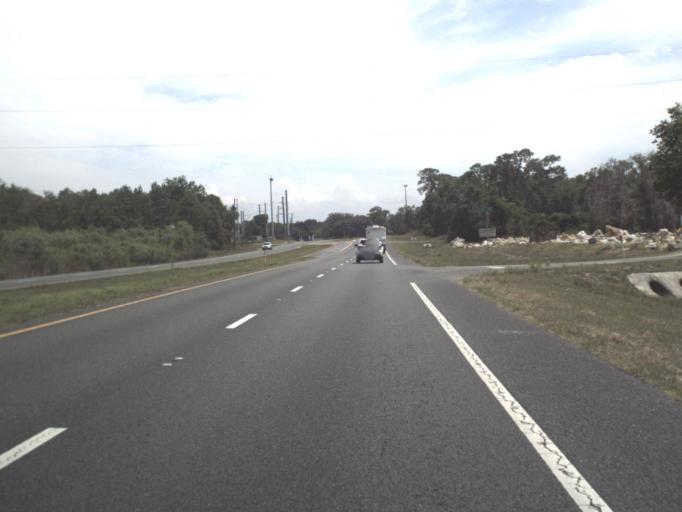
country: US
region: Florida
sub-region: Sumter County
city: Wildwood
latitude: 28.8271
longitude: -81.9926
